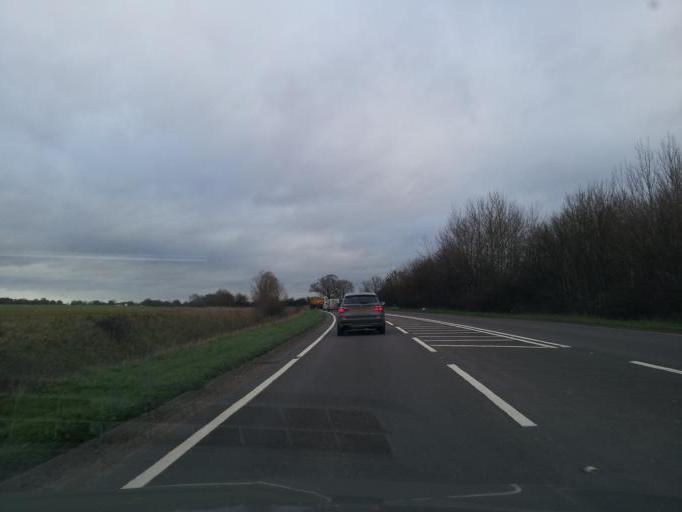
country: GB
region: England
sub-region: Norfolk
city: Long Stratton
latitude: 52.4101
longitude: 1.1941
